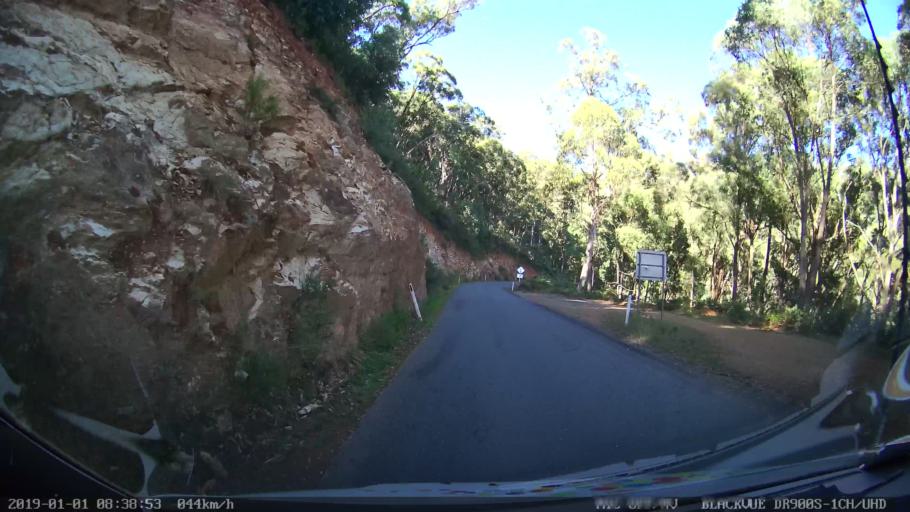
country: AU
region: New South Wales
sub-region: Snowy River
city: Jindabyne
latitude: -36.3329
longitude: 148.1952
